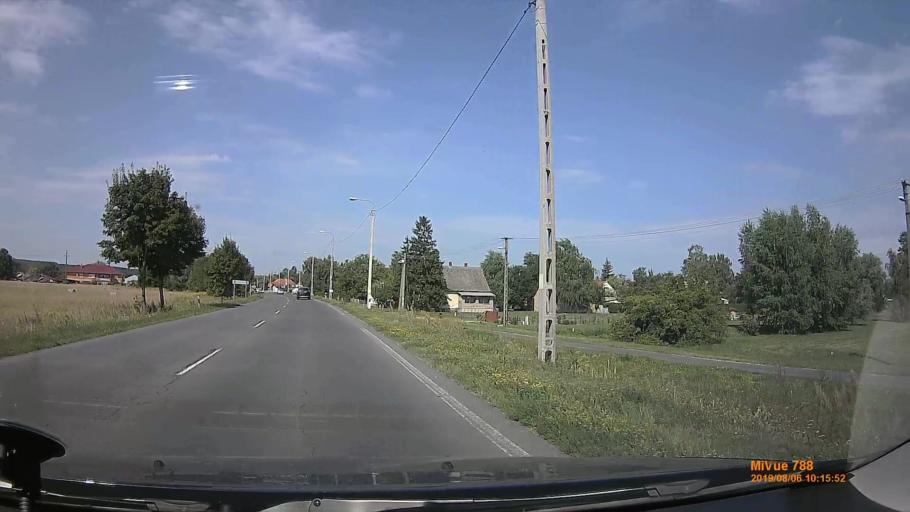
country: HU
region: Somogy
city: Kethely
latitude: 46.6997
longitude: 17.3868
